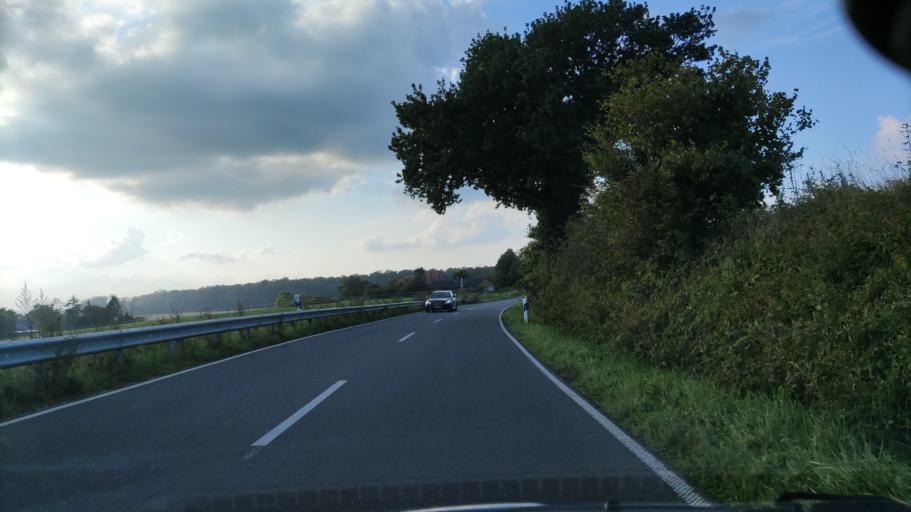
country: DE
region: Schleswig-Holstein
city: Glasau
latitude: 54.0385
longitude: 10.5407
